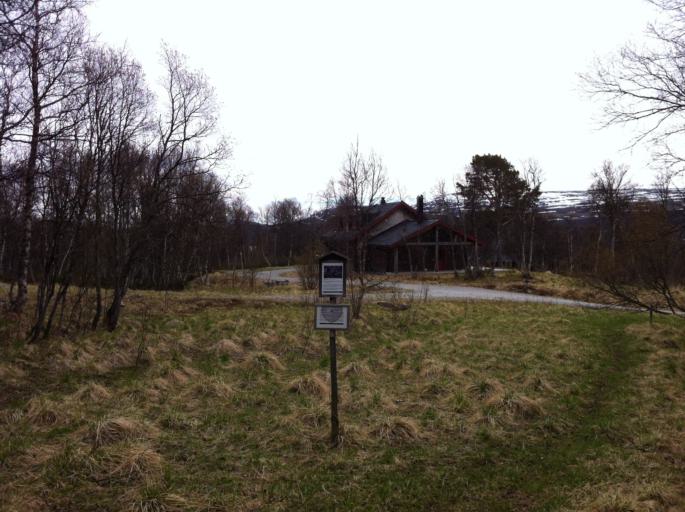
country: NO
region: Sor-Trondelag
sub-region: Tydal
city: Aas
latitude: 62.5534
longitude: 12.3148
